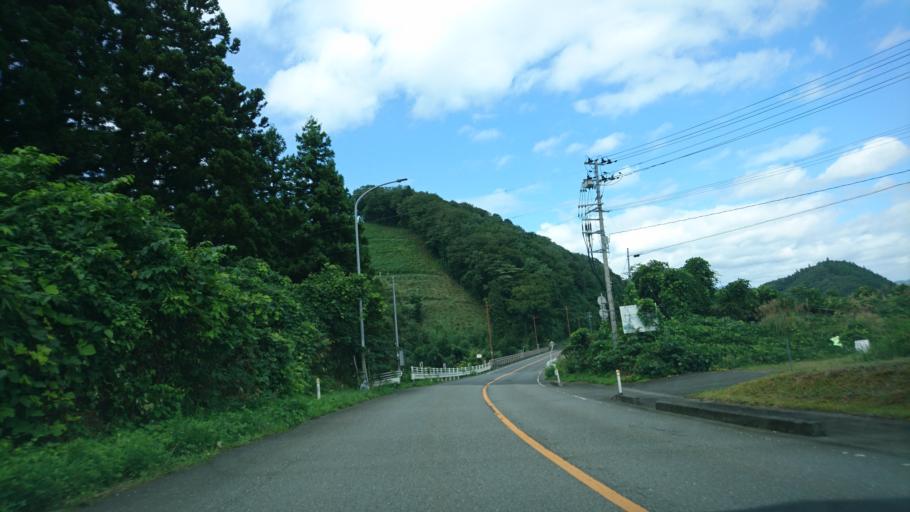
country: JP
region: Miyagi
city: Furukawa
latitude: 38.7754
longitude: 140.8577
